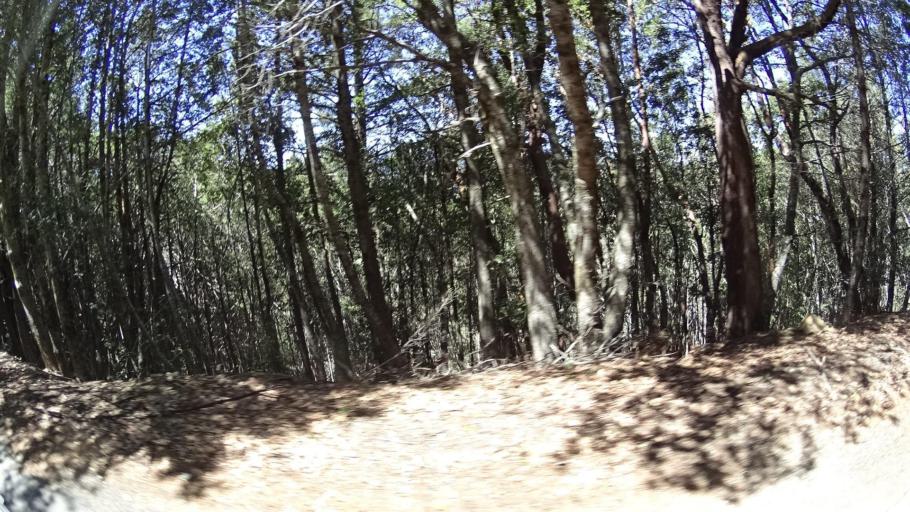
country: US
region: California
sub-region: Humboldt County
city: Rio Dell
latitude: 40.2852
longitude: -124.0601
